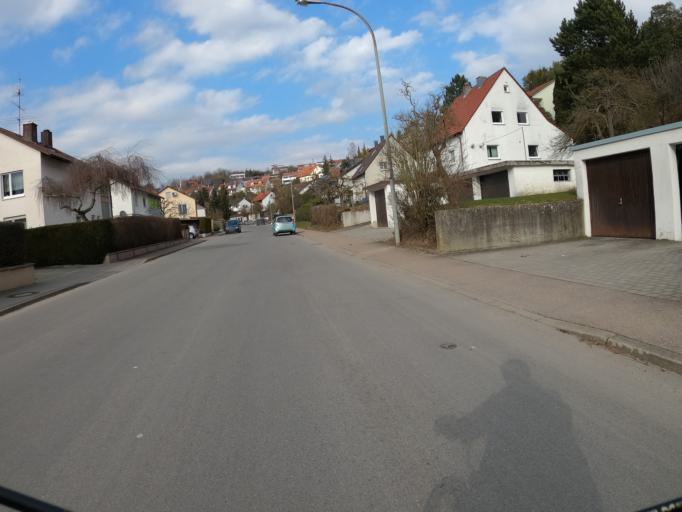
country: DE
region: Bavaria
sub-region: Swabia
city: Neu-Ulm
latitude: 48.4406
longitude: 10.0507
